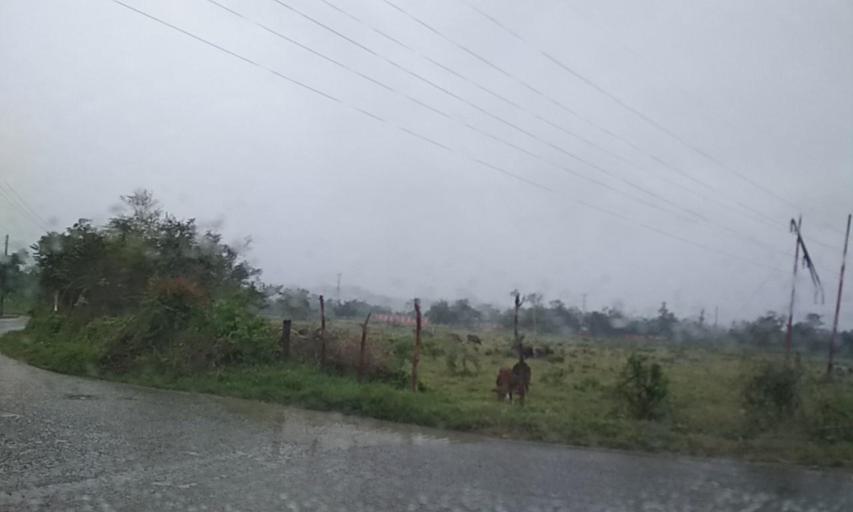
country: MX
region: Veracruz
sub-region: Papantla
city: El Chote
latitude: 20.4021
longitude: -97.3402
